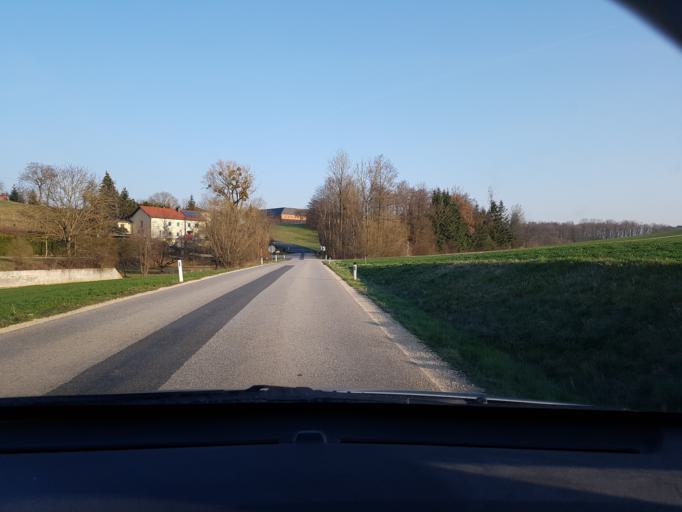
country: AT
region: Upper Austria
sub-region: Politischer Bezirk Linz-Land
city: Ansfelden
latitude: 48.1345
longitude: 14.2777
